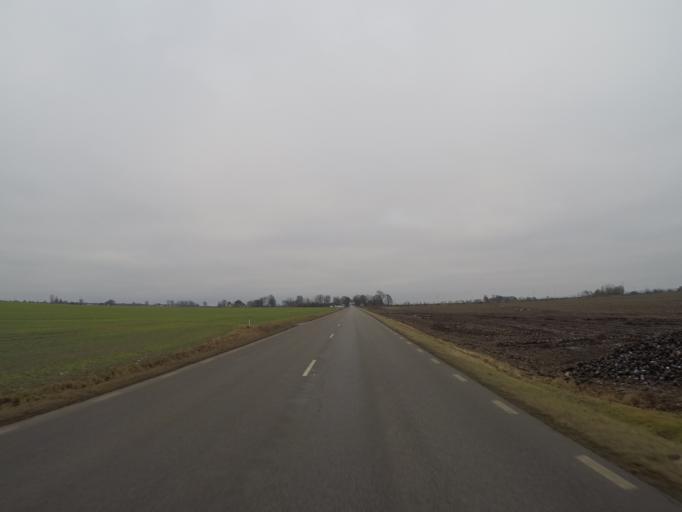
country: SE
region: Skane
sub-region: Hoors Kommun
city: Loberod
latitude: 55.7813
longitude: 13.4212
